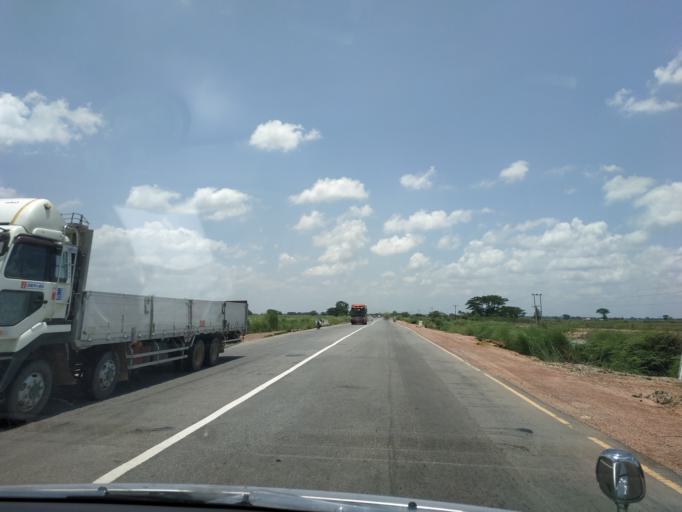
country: MM
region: Bago
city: Thanatpin
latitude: 17.4524
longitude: 96.6363
